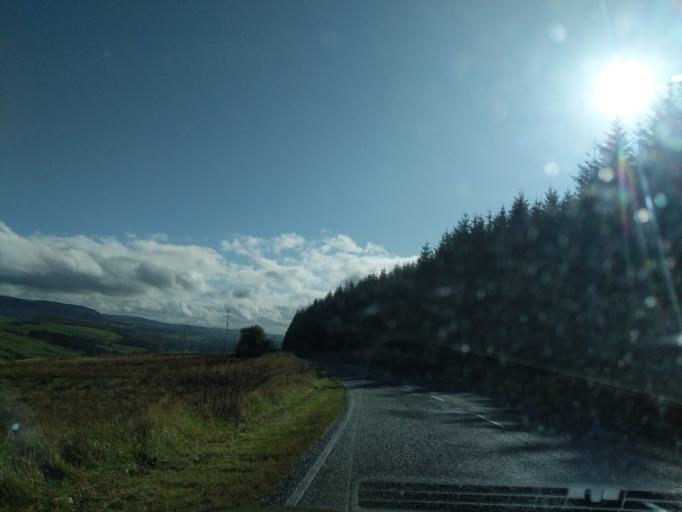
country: GB
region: Scotland
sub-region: Dumfries and Galloway
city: Moffat
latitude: 55.3719
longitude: -3.4768
